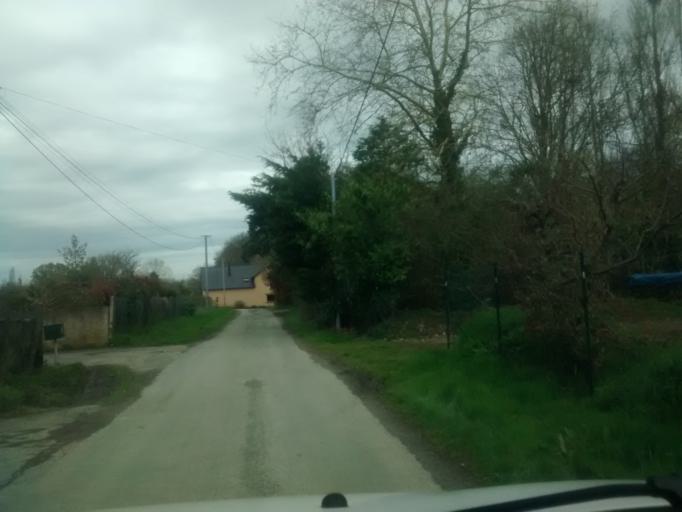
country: FR
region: Brittany
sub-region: Departement d'Ille-et-Vilaine
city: Saint-Sulpice-la-Foret
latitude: 48.2009
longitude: -1.6025
